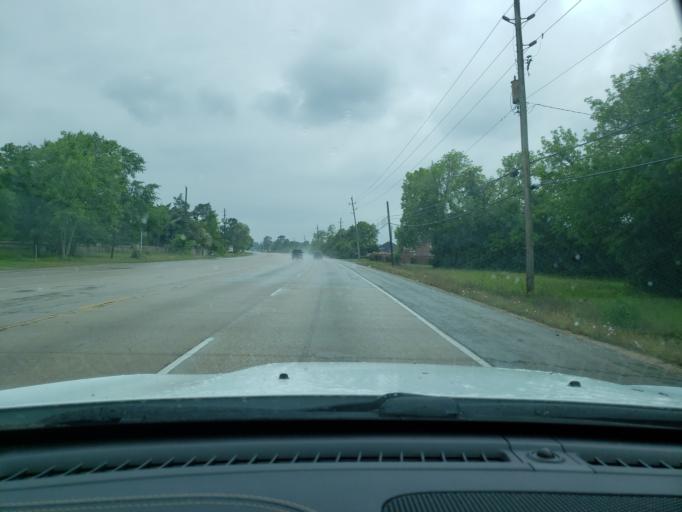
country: US
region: Texas
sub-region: Chambers County
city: Mont Belvieu
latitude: 29.7923
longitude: -94.9098
